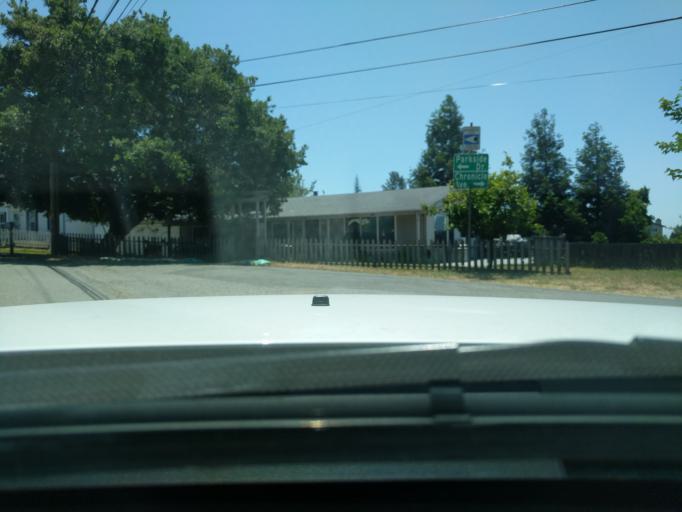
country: US
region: California
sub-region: Alameda County
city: Fairview
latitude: 37.6569
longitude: -122.0415
